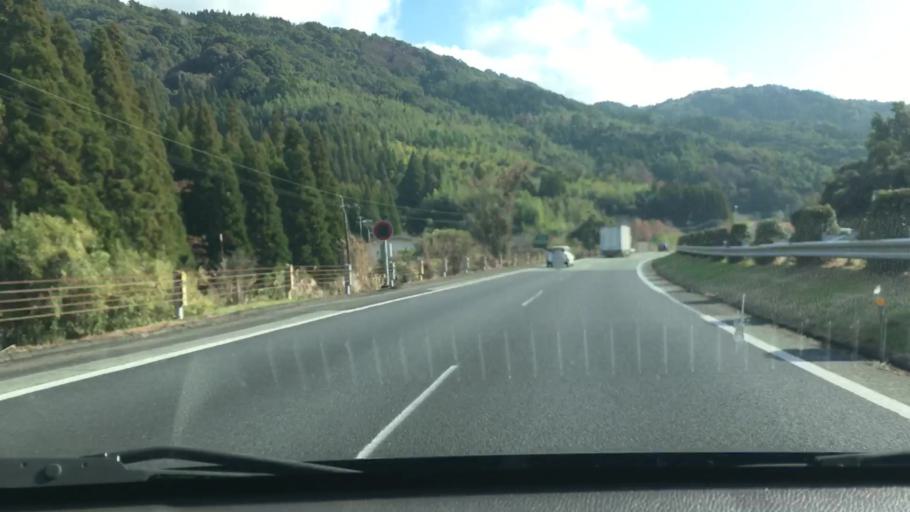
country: JP
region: Kumamoto
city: Matsubase
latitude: 32.6148
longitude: 130.7234
